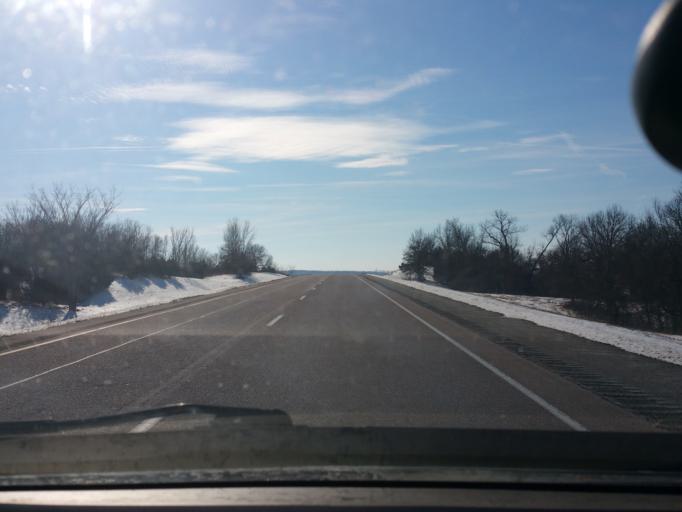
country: US
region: Iowa
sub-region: Decatur County
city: Leon
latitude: 40.6919
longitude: -93.8462
